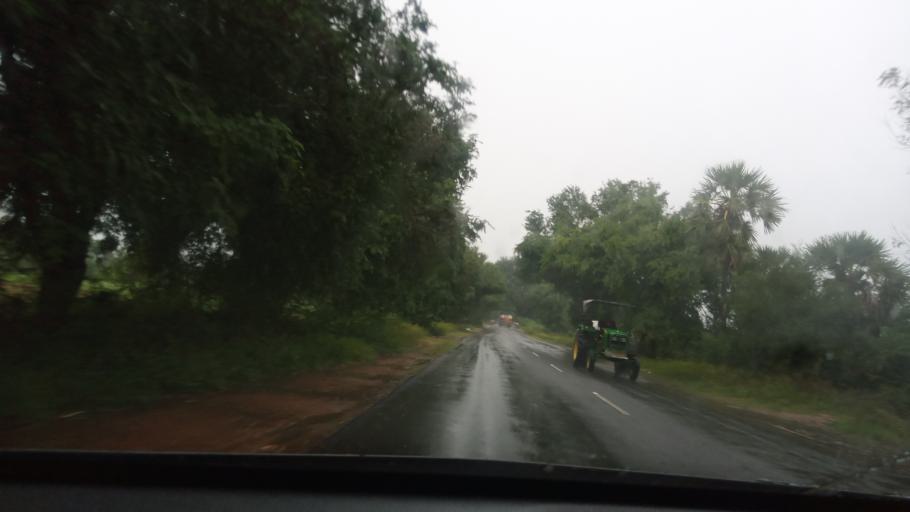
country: IN
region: Tamil Nadu
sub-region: Vellore
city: Kalavai
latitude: 12.8115
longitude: 79.4127
